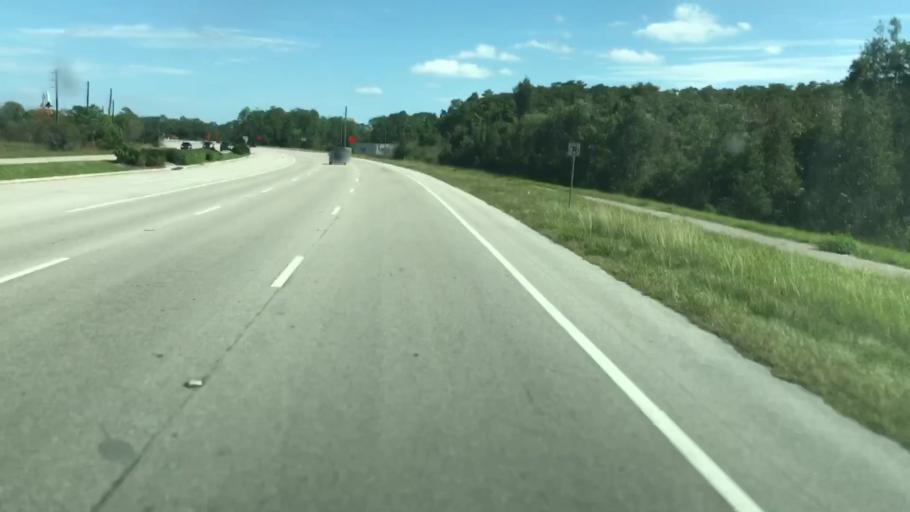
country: US
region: Florida
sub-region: Lee County
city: Gateway
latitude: 26.5476
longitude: -81.7654
